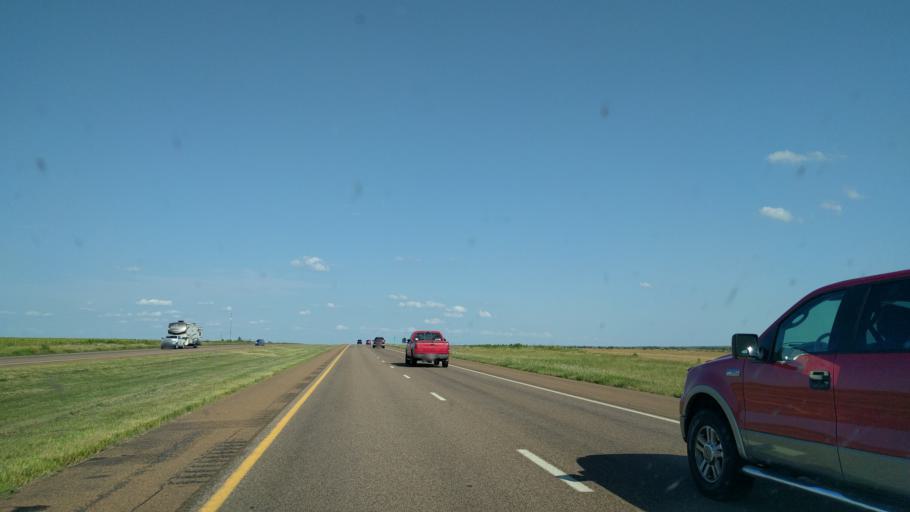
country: US
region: Kansas
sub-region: Ellis County
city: Ellis
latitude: 38.9602
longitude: -99.6267
